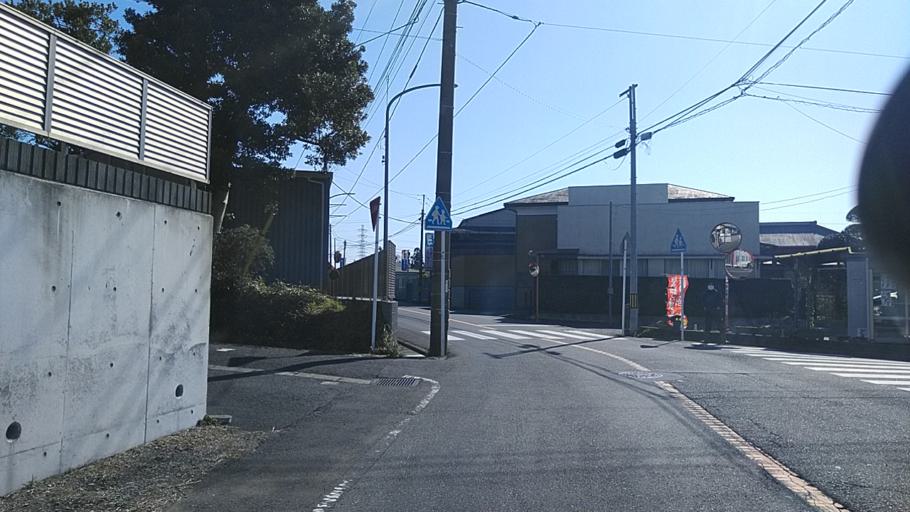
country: JP
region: Kanagawa
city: Fujisawa
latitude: 35.4106
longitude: 139.4782
